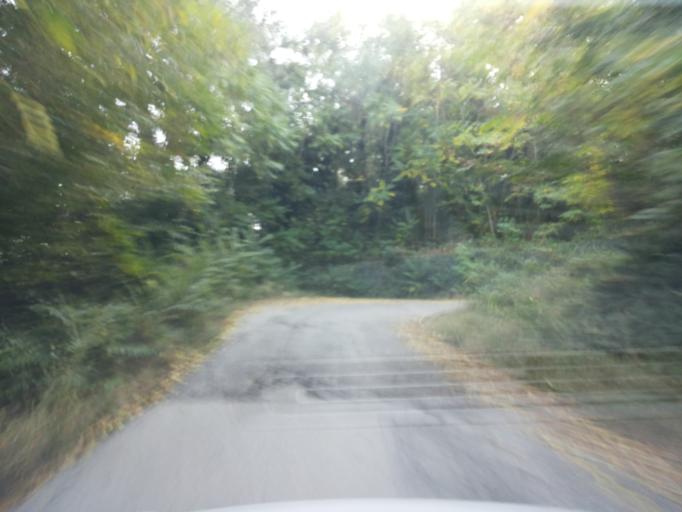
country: IT
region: Piedmont
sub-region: Provincia di Torino
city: Banchette
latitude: 45.4525
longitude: 7.8656
